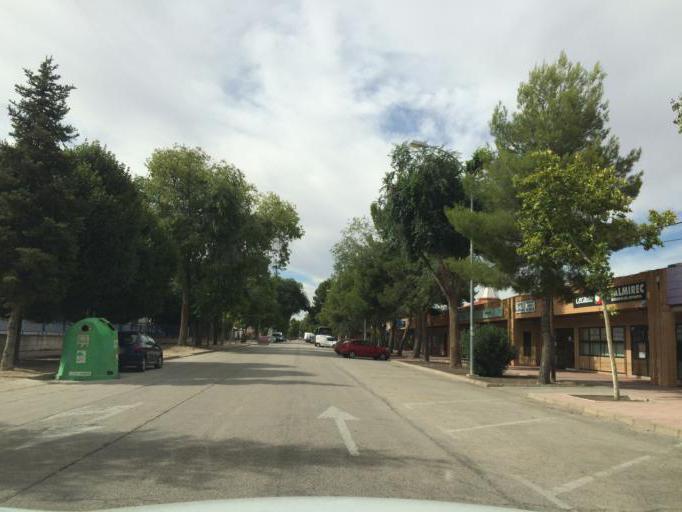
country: ES
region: Castille-La Mancha
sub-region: Provincia de Albacete
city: Albacete
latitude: 39.0115
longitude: -1.8780
